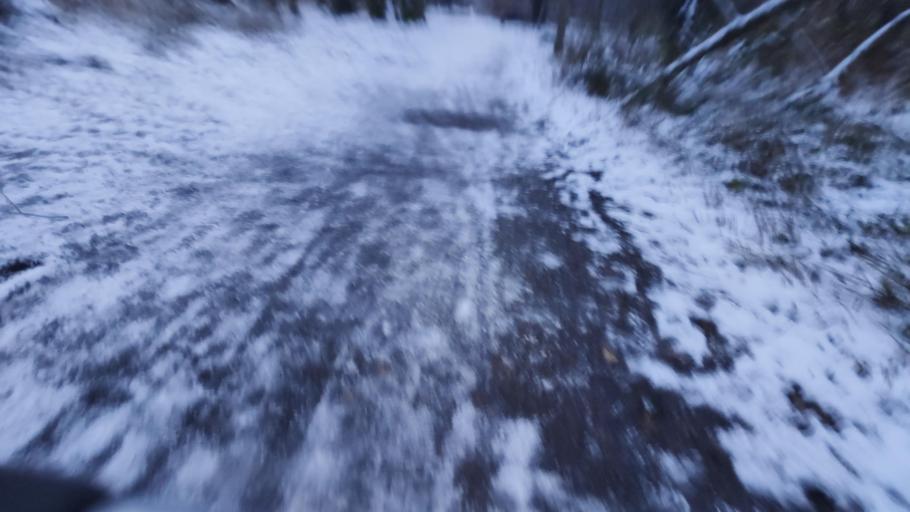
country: PL
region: Lower Silesian Voivodeship
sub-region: Powiat wroclawski
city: Bielany Wroclawskie
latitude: 51.0866
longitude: 16.9775
